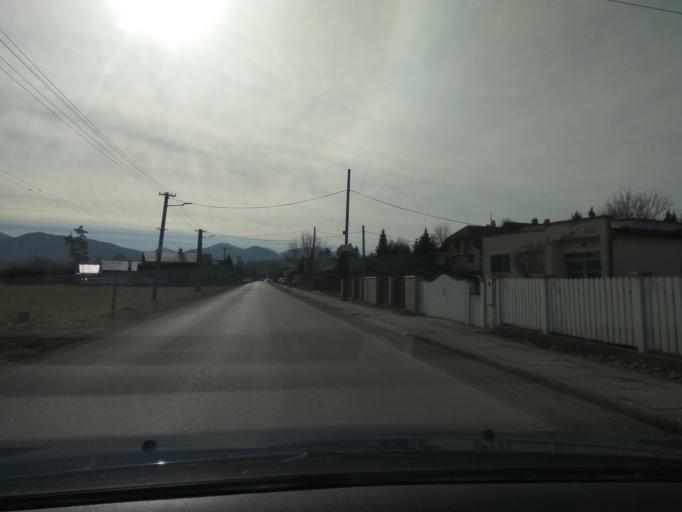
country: SK
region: Zilinsky
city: Rajec
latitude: 49.1237
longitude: 18.6730
